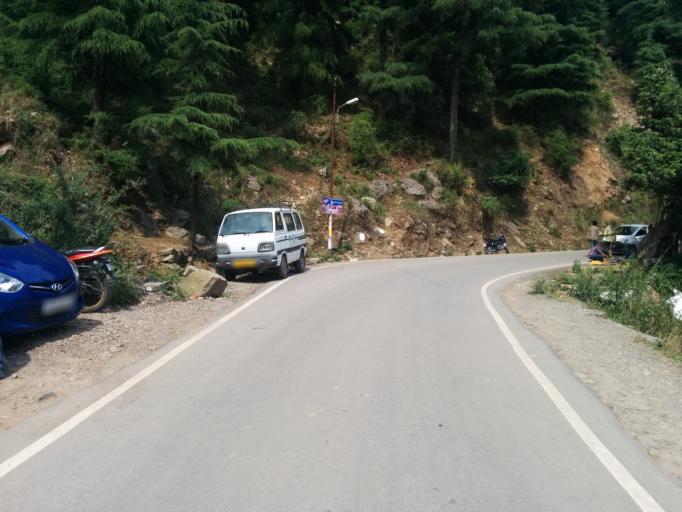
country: IN
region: Himachal Pradesh
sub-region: Kangra
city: Dharmsala
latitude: 32.2397
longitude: 76.3299
